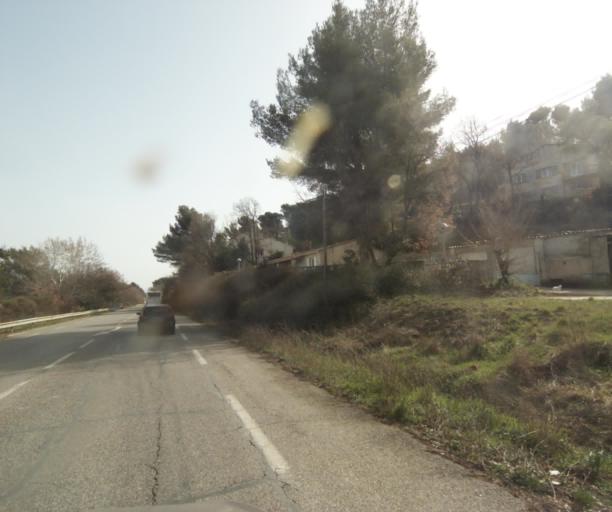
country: FR
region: Provence-Alpes-Cote d'Azur
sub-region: Departement des Bouches-du-Rhone
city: Mimet
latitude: 43.4187
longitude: 5.5113
